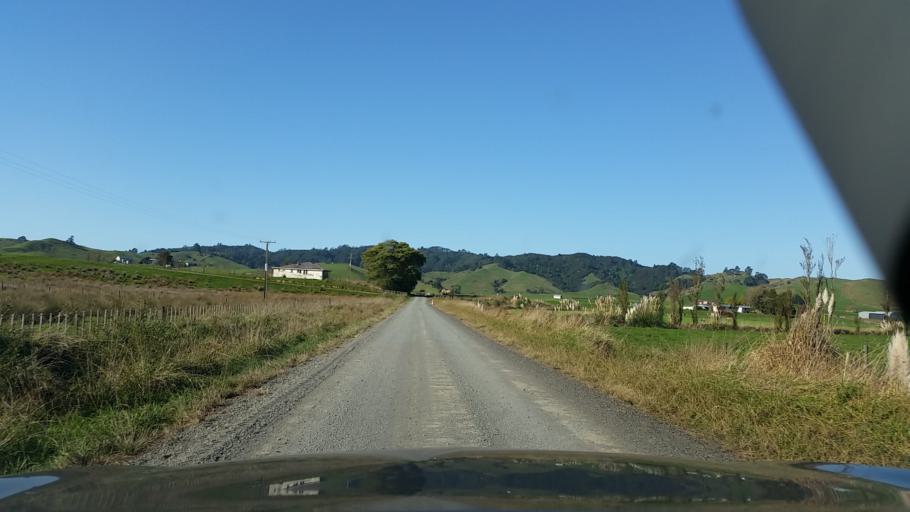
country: NZ
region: Waikato
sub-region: Hamilton City
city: Hamilton
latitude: -37.5704
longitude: 175.4173
